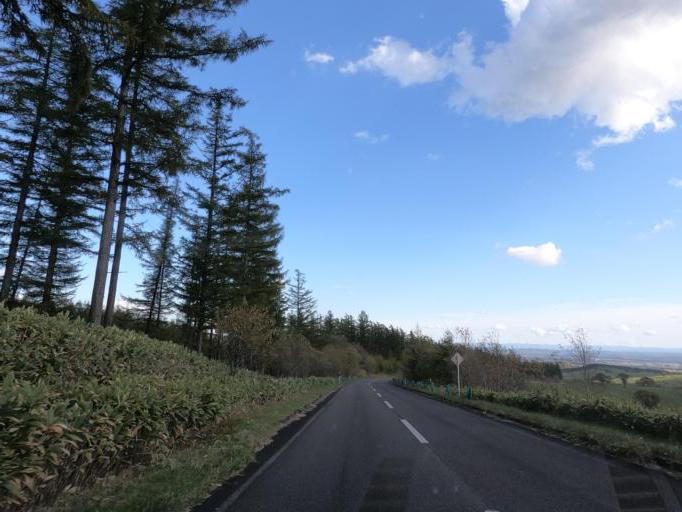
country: JP
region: Hokkaido
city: Otofuke
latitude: 43.2899
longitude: 143.2121
